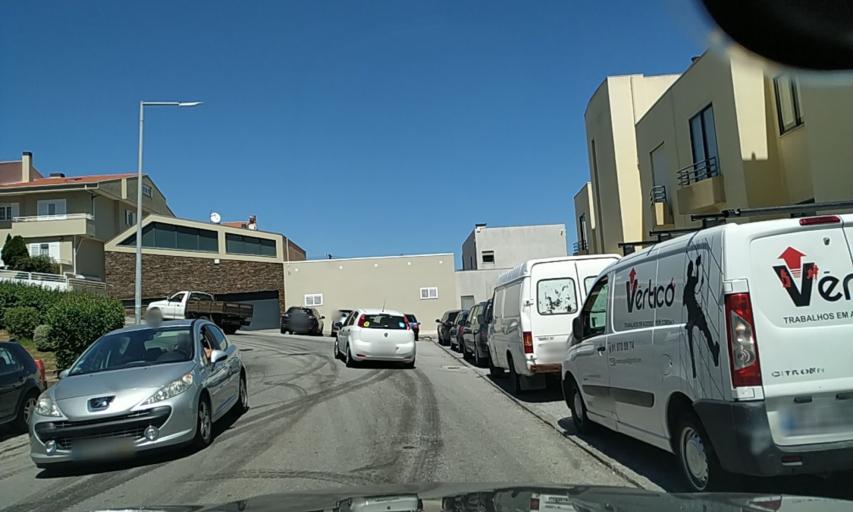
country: PT
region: Porto
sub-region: Vila Nova de Gaia
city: Canidelo
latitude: 41.1372
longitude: -8.6433
